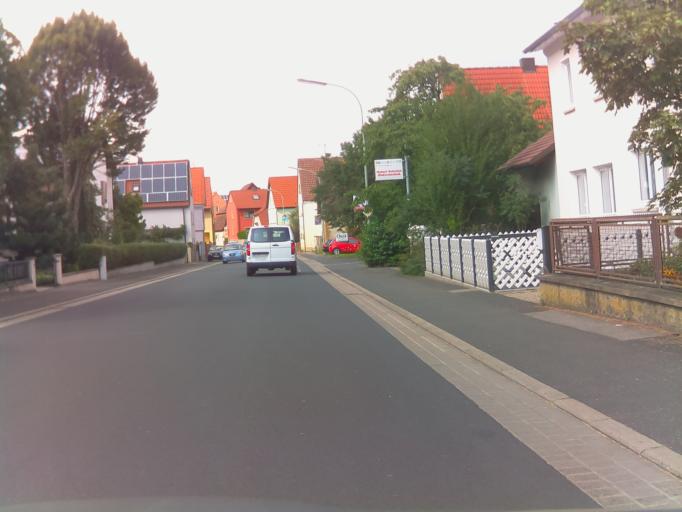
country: DE
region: Bavaria
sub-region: Regierungsbezirk Unterfranken
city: Schwebheim
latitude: 49.9882
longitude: 10.2488
